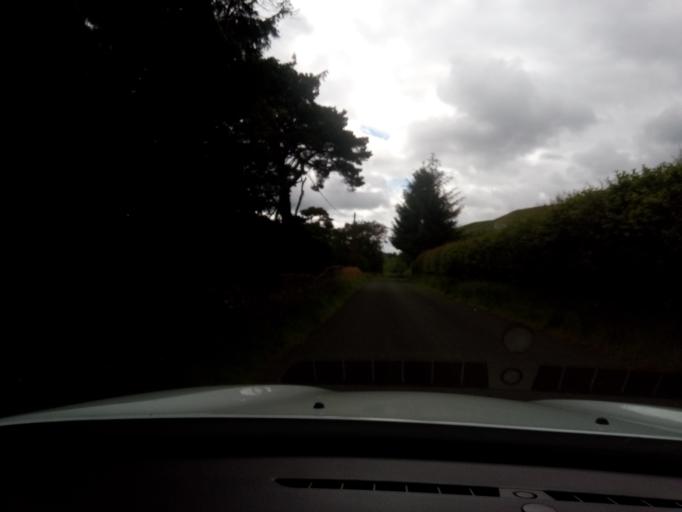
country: GB
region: Scotland
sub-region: The Scottish Borders
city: Innerleithen
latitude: 55.4522
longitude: -3.1019
